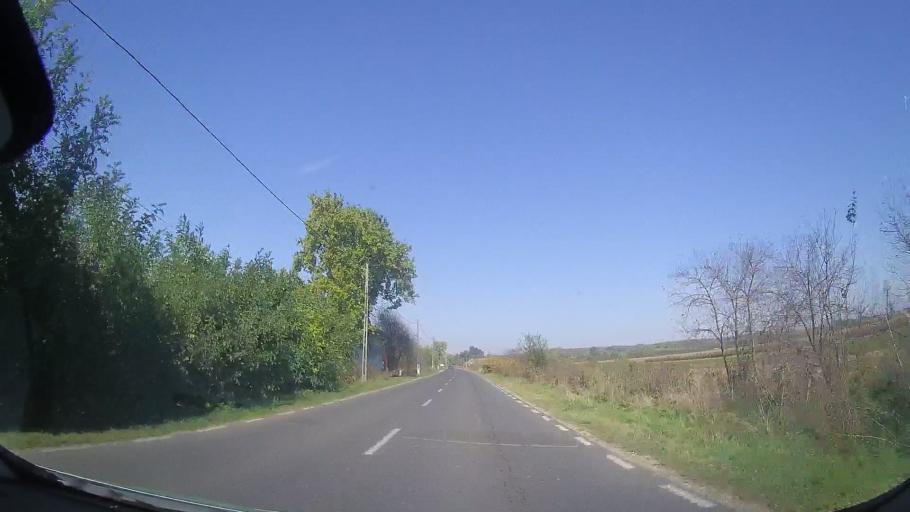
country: RO
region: Timis
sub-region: Comuna Balint
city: Balint
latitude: 45.8061
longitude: 21.8609
